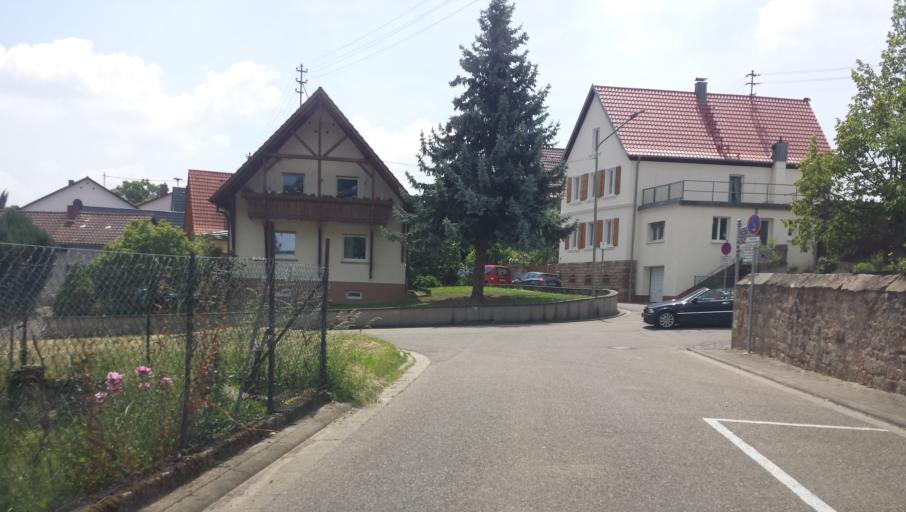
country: DE
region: Rheinland-Pfalz
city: Gleiszellen-Gleishorbach
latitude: 49.1299
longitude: 8.0081
